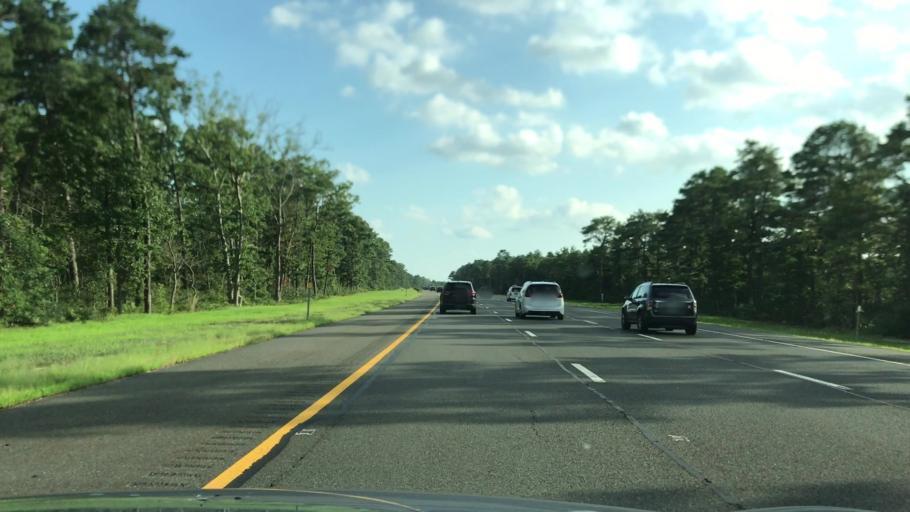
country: US
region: New Jersey
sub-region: Ocean County
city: Manahawkin
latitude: 39.6894
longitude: -74.3006
